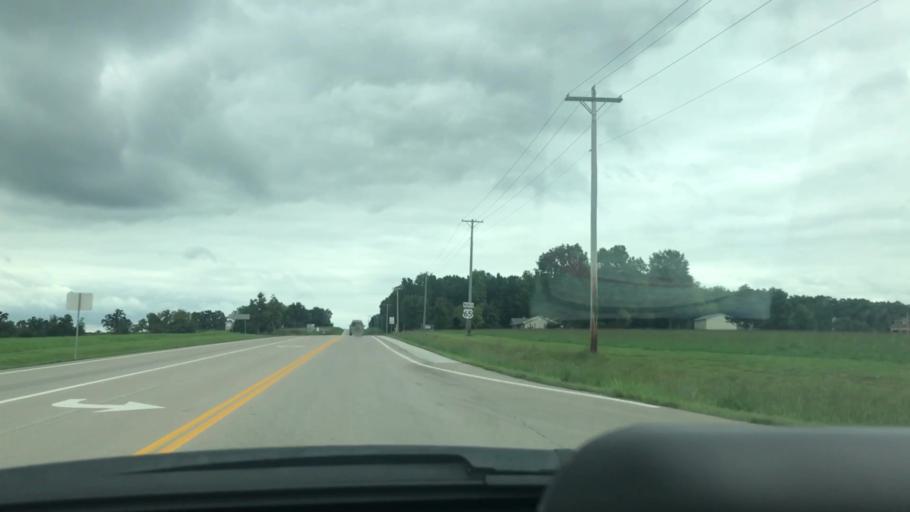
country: US
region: Missouri
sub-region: Dallas County
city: Buffalo
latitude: 37.6680
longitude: -93.1033
